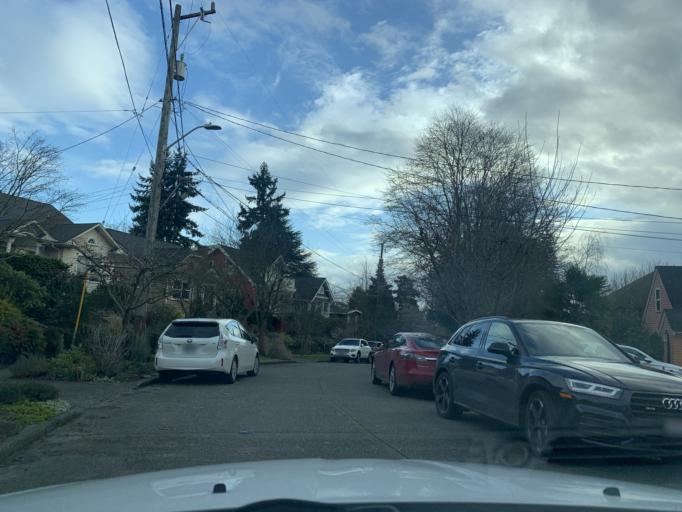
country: US
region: Washington
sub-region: King County
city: Seattle
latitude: 47.6714
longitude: -122.2974
